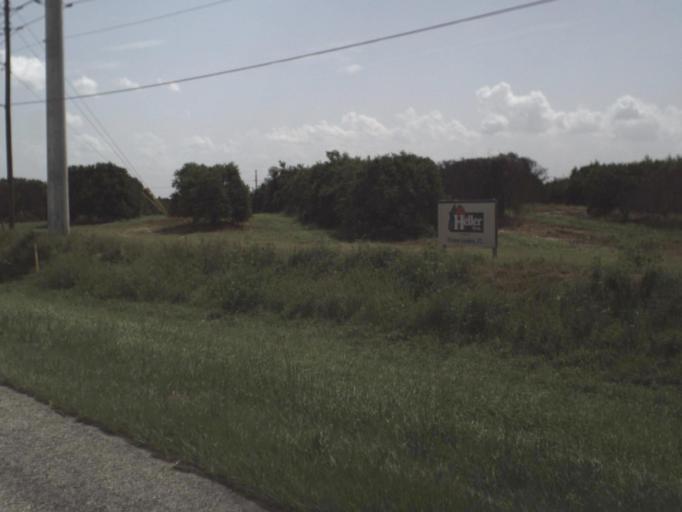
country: US
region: Florida
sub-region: Polk County
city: Davenport
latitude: 28.2212
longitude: -81.6433
